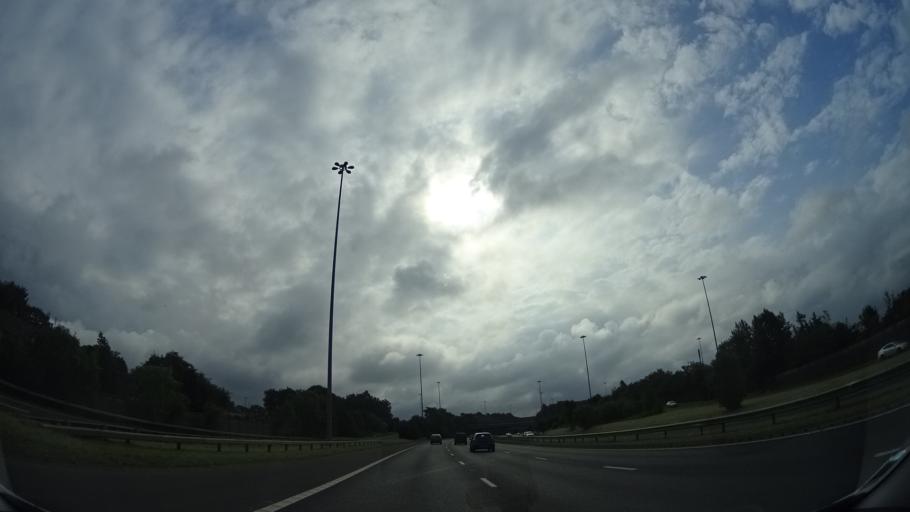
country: GB
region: England
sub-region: Knowsley
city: Huyton
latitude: 53.4085
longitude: -2.8730
